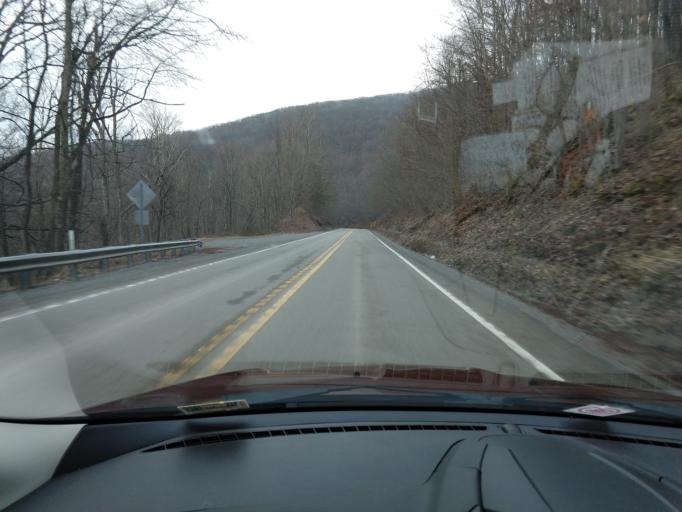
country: US
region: West Virginia
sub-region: Randolph County
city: Elkins
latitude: 38.6409
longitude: -79.9245
